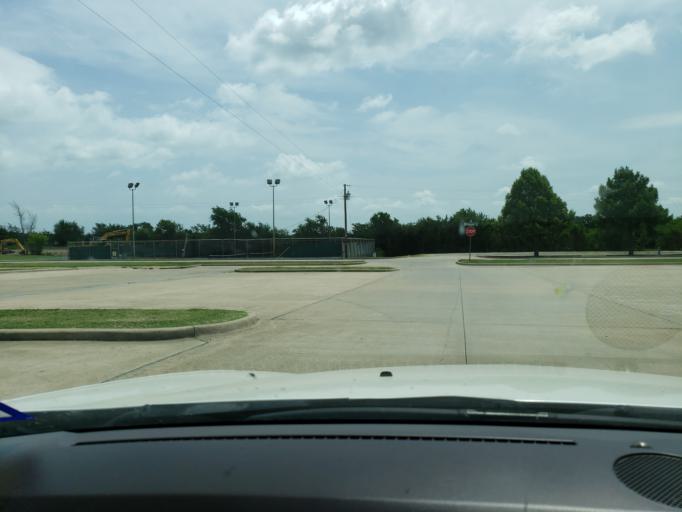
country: US
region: Texas
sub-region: Dallas County
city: Rowlett
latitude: 32.9000
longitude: -96.5599
